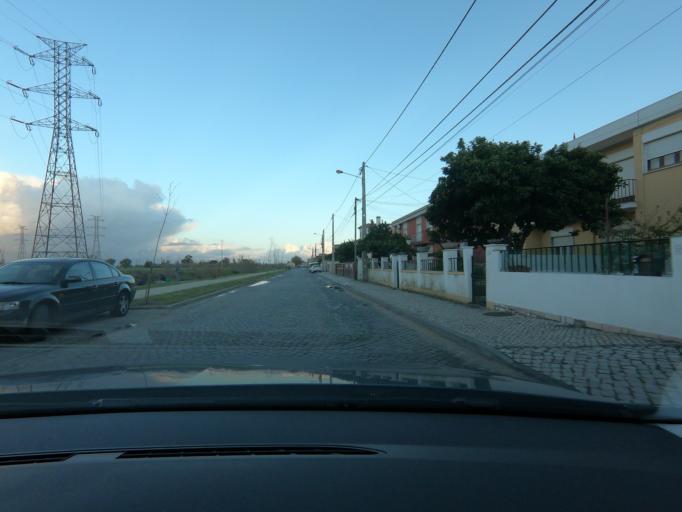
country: PT
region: Lisbon
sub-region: Vila Franca de Xira
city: Castanheira do Ribatejo
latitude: 39.0089
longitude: -8.9563
